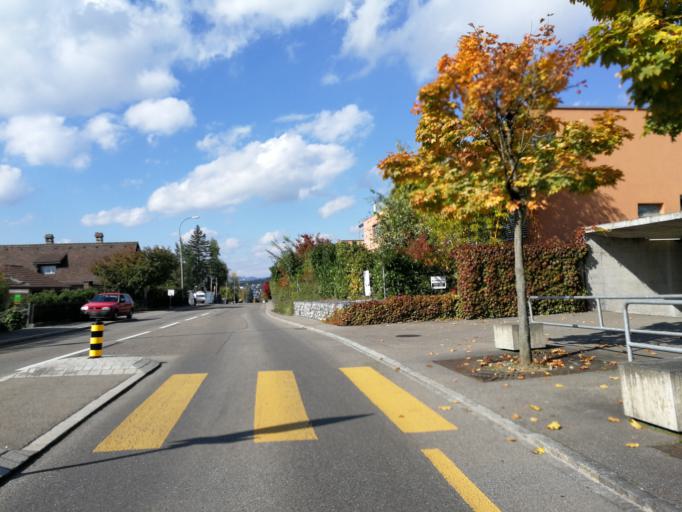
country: CH
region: Zurich
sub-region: Bezirk Meilen
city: Maennedorf / Dorfkern
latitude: 47.2602
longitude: 8.6918
